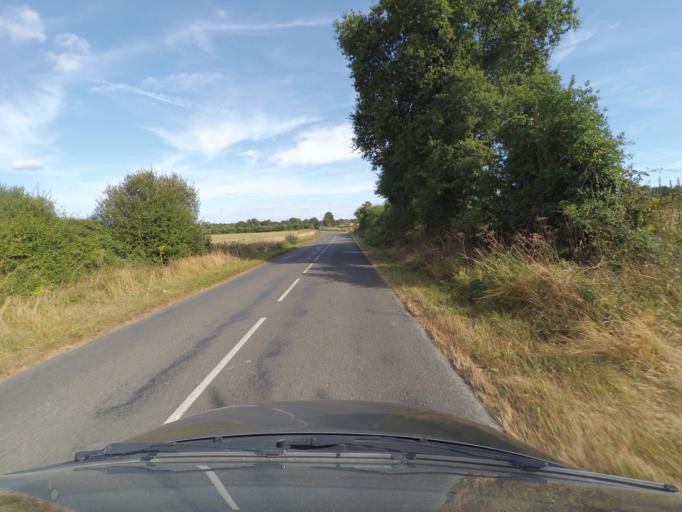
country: FR
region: Pays de la Loire
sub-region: Departement de la Loire-Atlantique
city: Montbert
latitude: 47.0435
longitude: -1.4770
